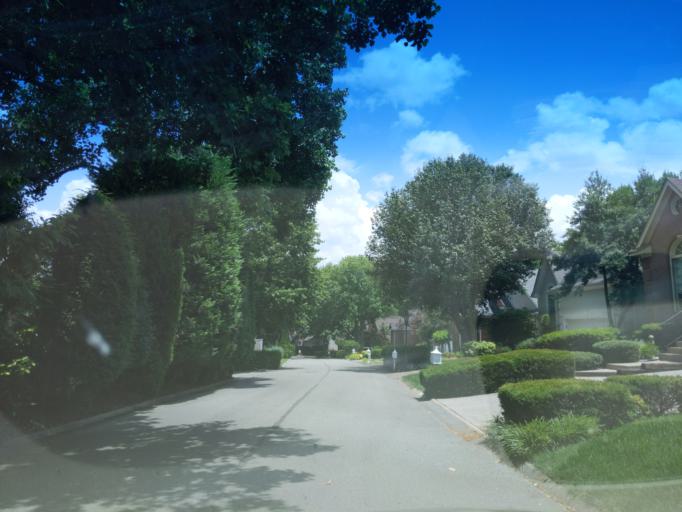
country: US
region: Tennessee
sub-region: Williamson County
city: Brentwood
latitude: 36.0437
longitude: -86.7678
